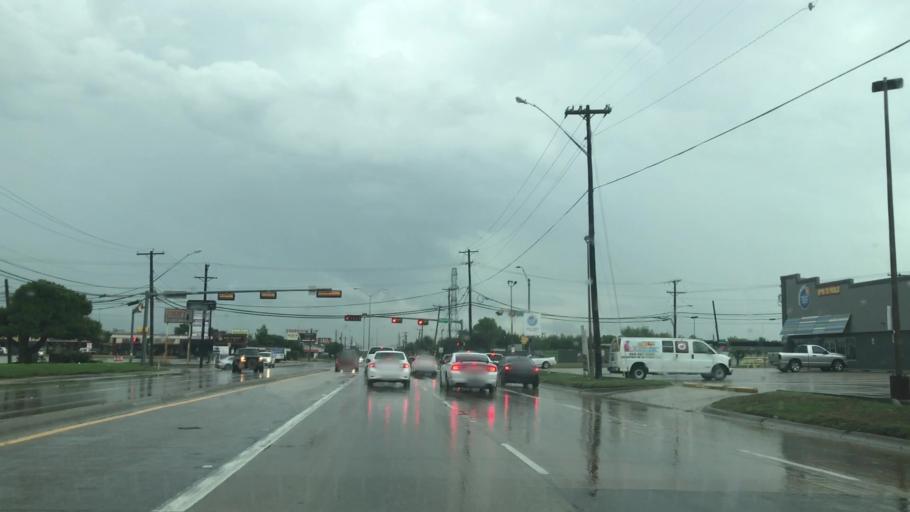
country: US
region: Texas
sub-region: Dallas County
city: Farmers Branch
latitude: 32.8674
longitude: -96.9087
